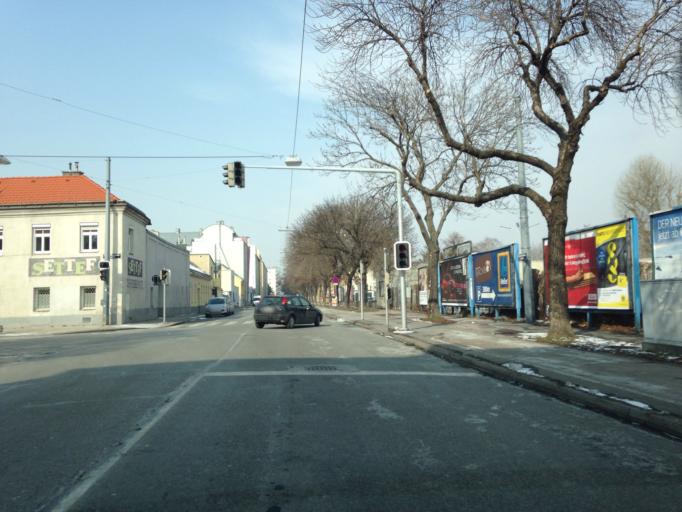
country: AT
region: Vienna
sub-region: Wien Stadt
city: Vienna
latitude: 48.2315
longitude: 16.3784
